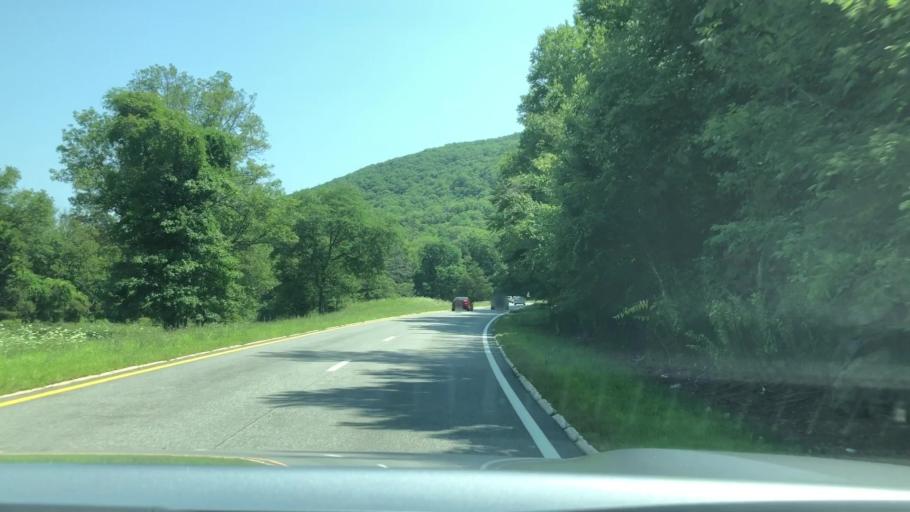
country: US
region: New York
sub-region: Orange County
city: Fort Montgomery
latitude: 41.3119
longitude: -74.0210
